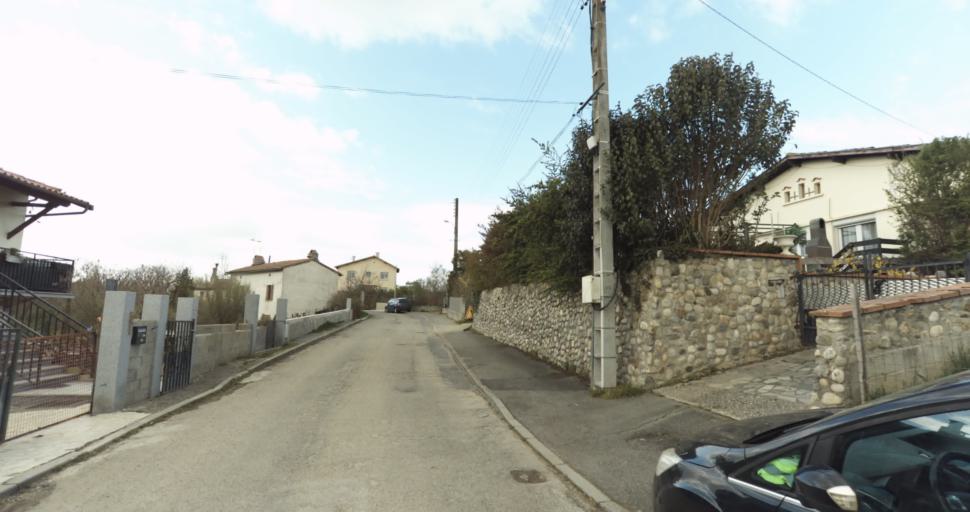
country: FR
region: Midi-Pyrenees
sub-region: Departement de la Haute-Garonne
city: Auterive
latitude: 43.3524
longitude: 1.4817
